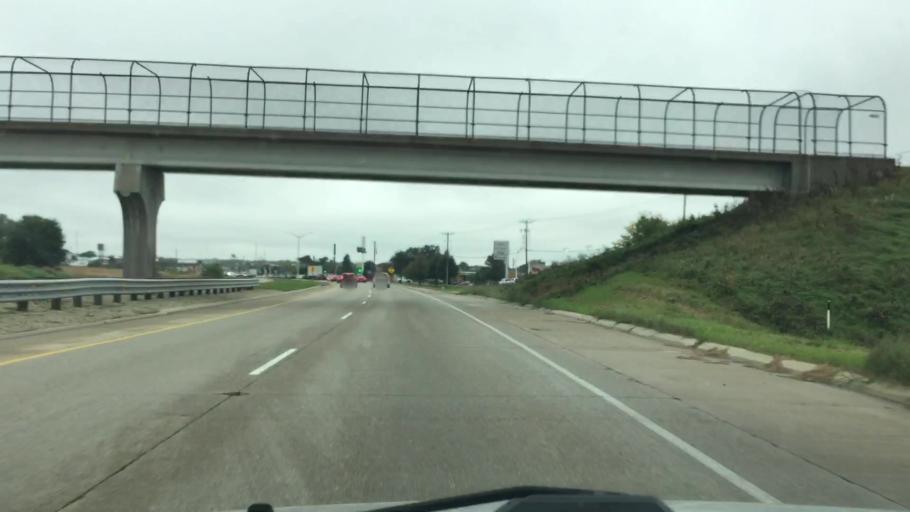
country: US
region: Wisconsin
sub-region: Rock County
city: Janesville
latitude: 42.7325
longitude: -88.9884
